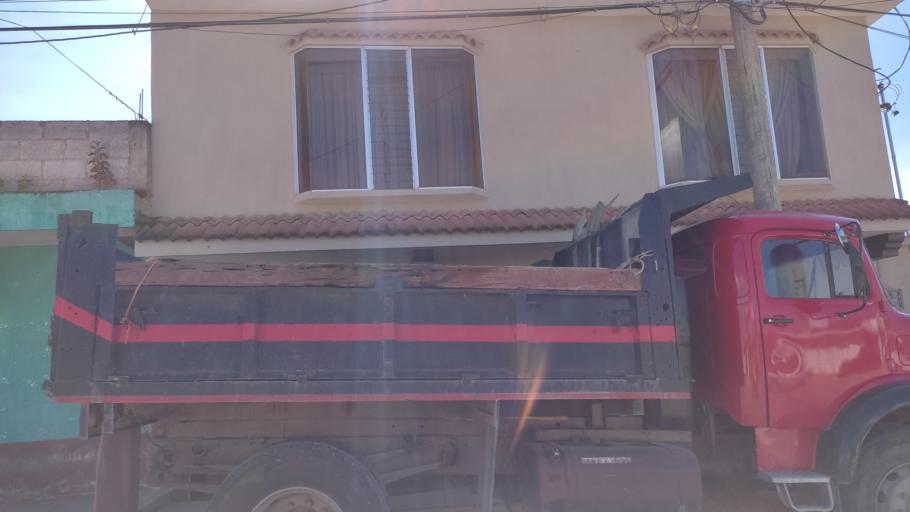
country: GT
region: Quetzaltenango
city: Quetzaltenango
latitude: 14.8537
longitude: -91.5237
